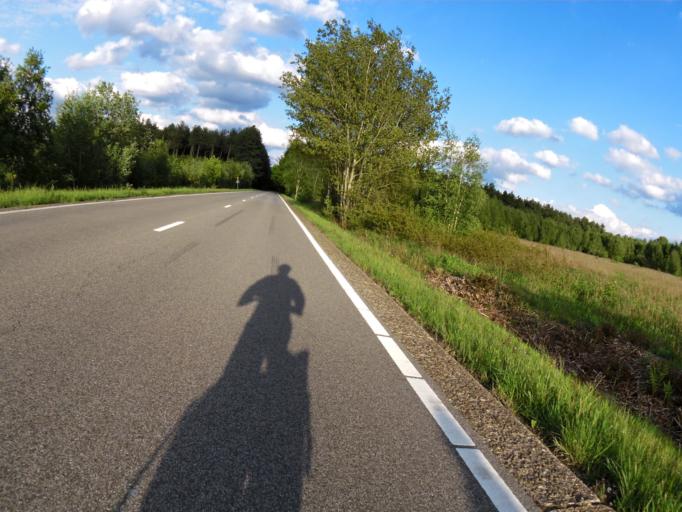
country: BE
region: Flanders
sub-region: Provincie Limburg
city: Zutendaal
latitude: 50.9546
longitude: 5.6226
